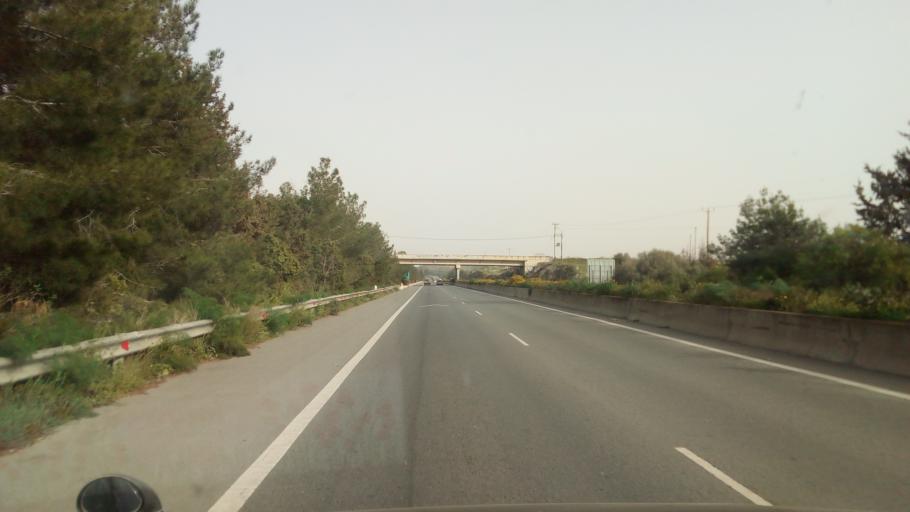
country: CY
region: Lefkosia
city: Lympia
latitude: 34.9948
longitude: 33.4456
